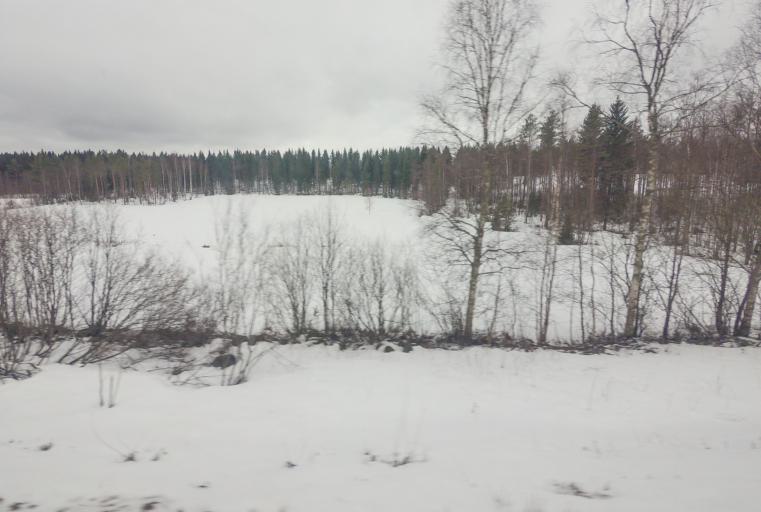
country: FI
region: Southern Savonia
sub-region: Savonlinna
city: Savonlinna
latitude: 61.8694
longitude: 29.0809
